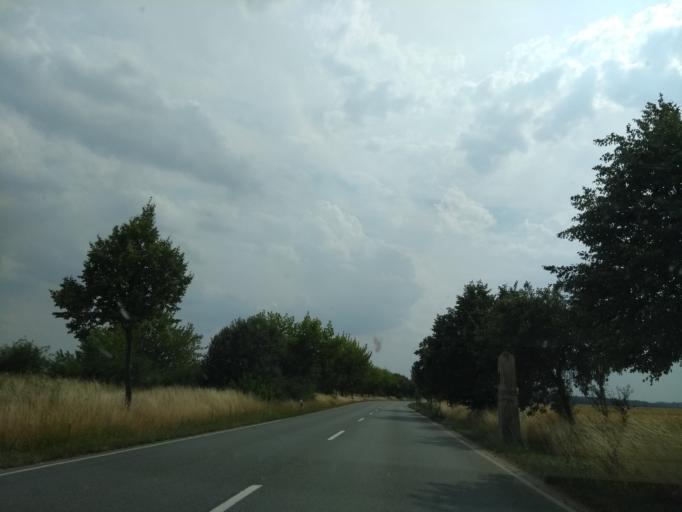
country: DE
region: Thuringia
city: Hirschfeld
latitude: 50.9794
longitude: 12.1354
